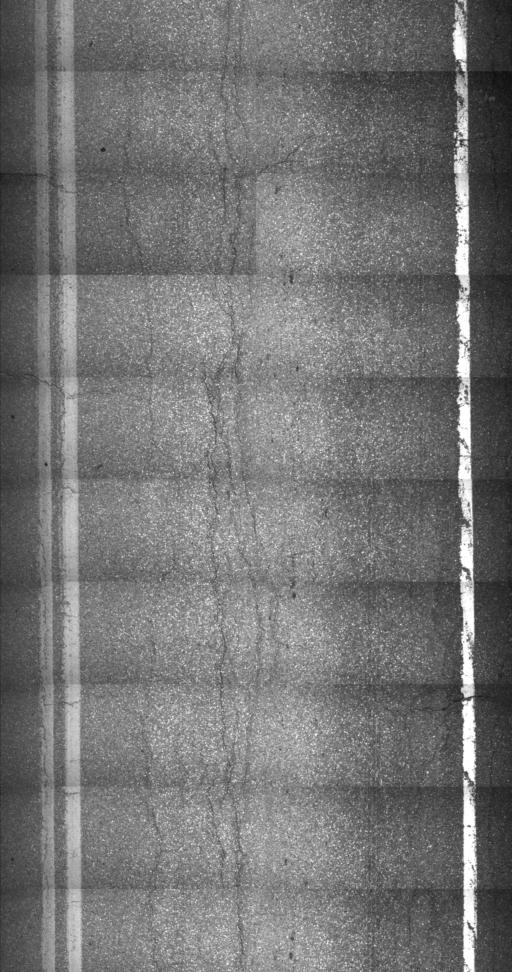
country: US
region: Vermont
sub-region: Addison County
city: Middlebury (village)
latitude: 43.9749
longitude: -73.1063
